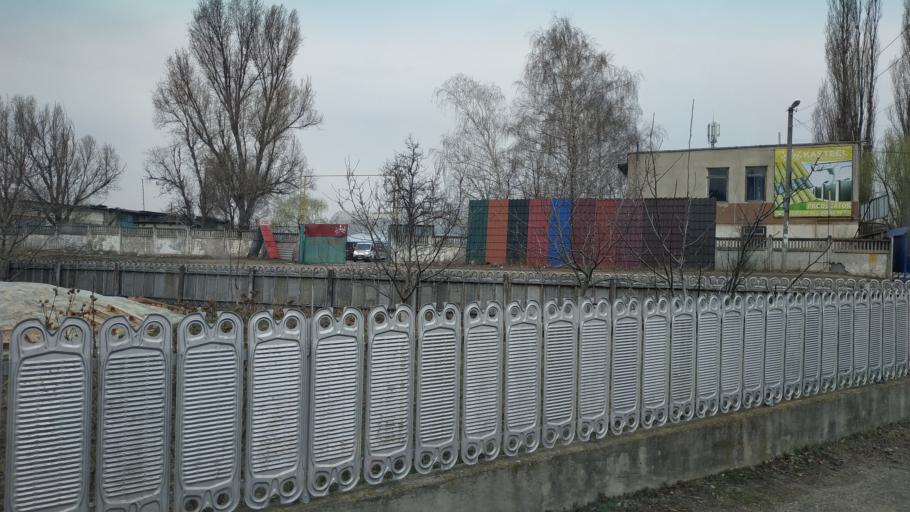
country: MD
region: Chisinau
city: Singera
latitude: 46.9123
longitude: 28.9720
